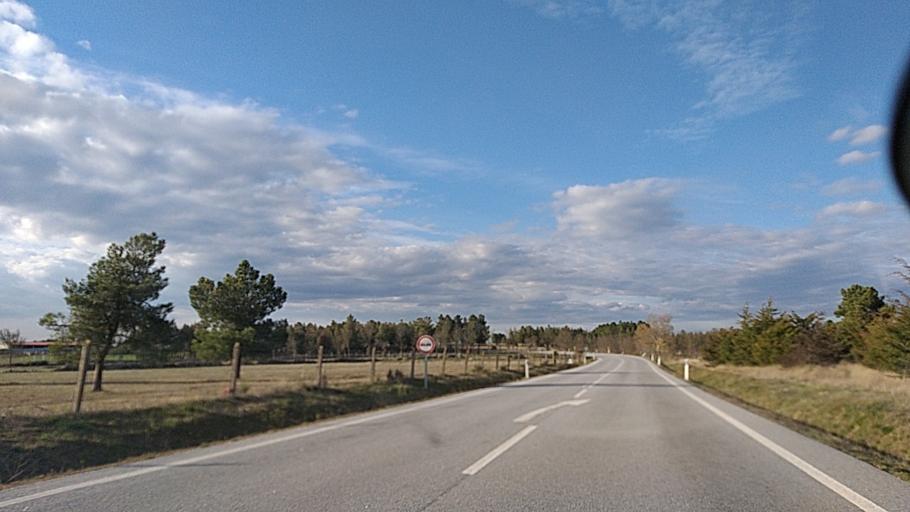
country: ES
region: Castille and Leon
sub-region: Provincia de Salamanca
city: Aldea del Obispo
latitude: 40.6682
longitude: -6.8589
